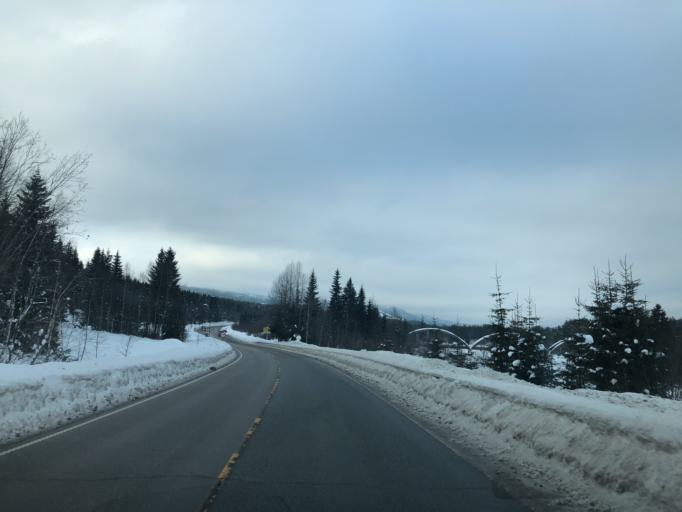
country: NO
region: Hedmark
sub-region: Trysil
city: Innbygda
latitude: 61.2695
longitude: 12.3036
